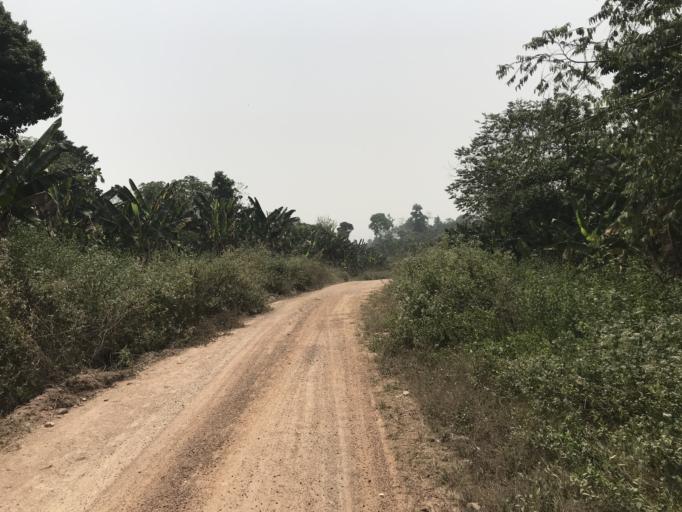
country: NG
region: Osun
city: Ifetedo
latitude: 7.0479
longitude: 4.4776
